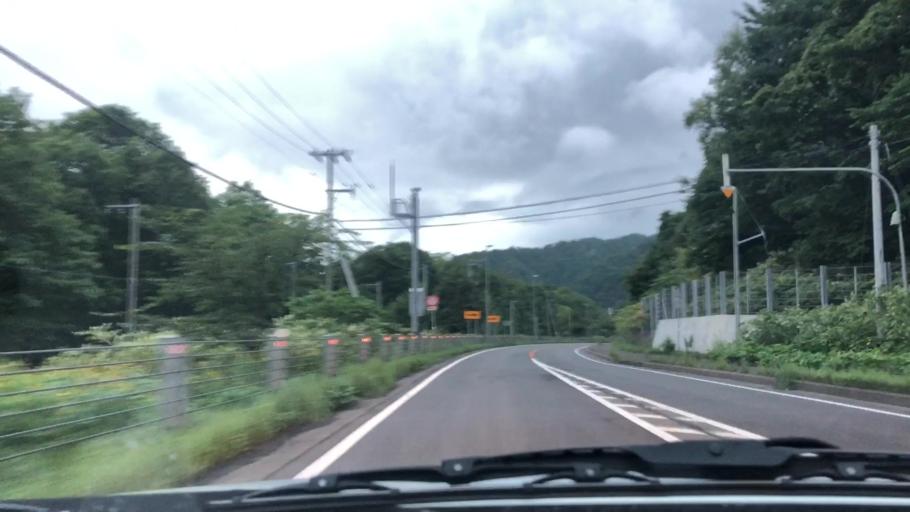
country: JP
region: Hokkaido
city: Chitose
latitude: 42.9134
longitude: 141.9667
